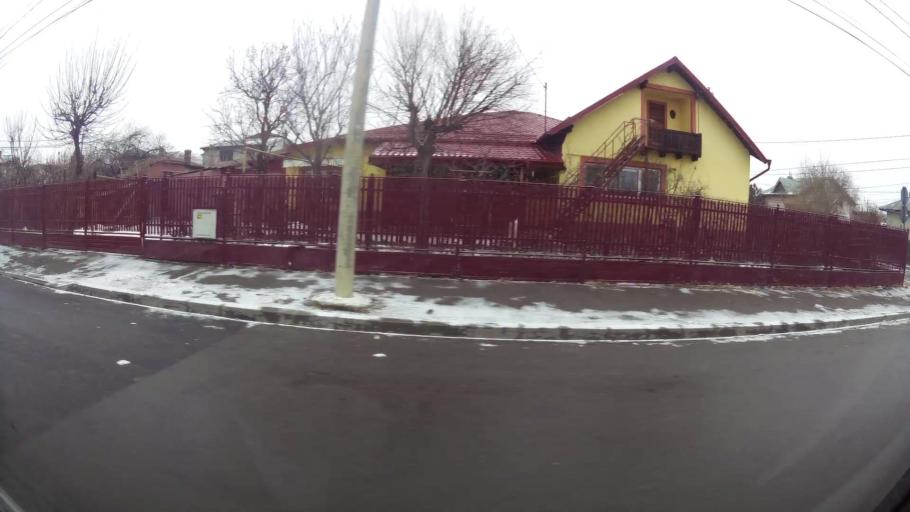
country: RO
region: Prahova
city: Ploiesti
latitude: 44.9529
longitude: 26.0400
